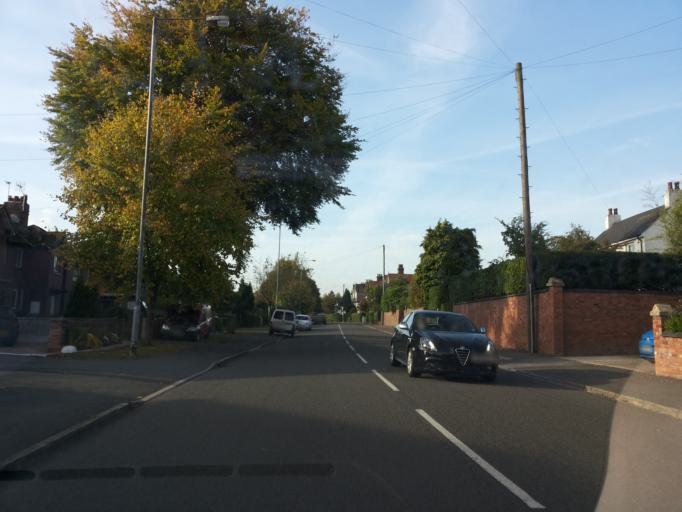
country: GB
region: England
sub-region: Staffordshire
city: Stone
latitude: 52.9072
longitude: -2.1588
